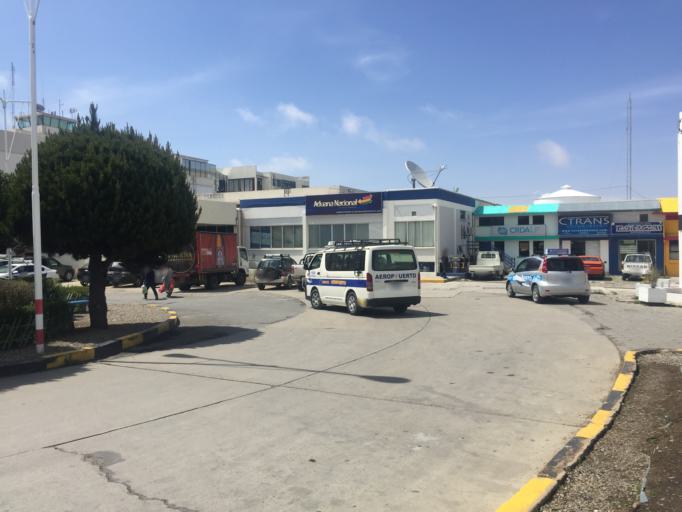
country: BO
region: La Paz
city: La Paz
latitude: -16.5082
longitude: -68.1775
